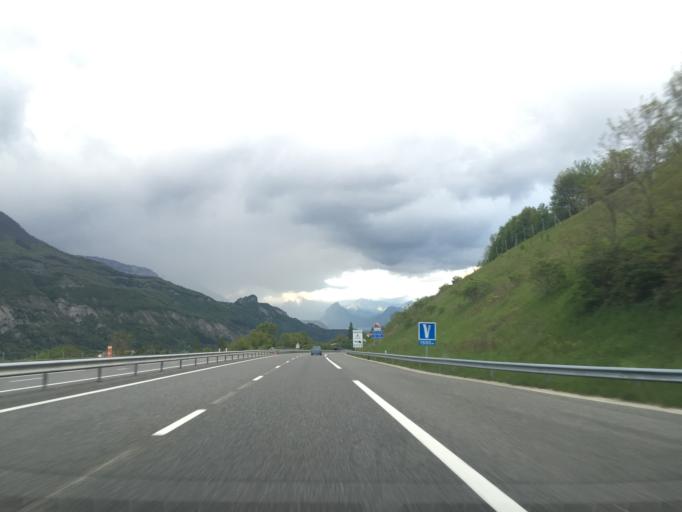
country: FR
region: Rhone-Alpes
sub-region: Departement de l'Isere
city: Vif
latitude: 45.0200
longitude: 5.6614
